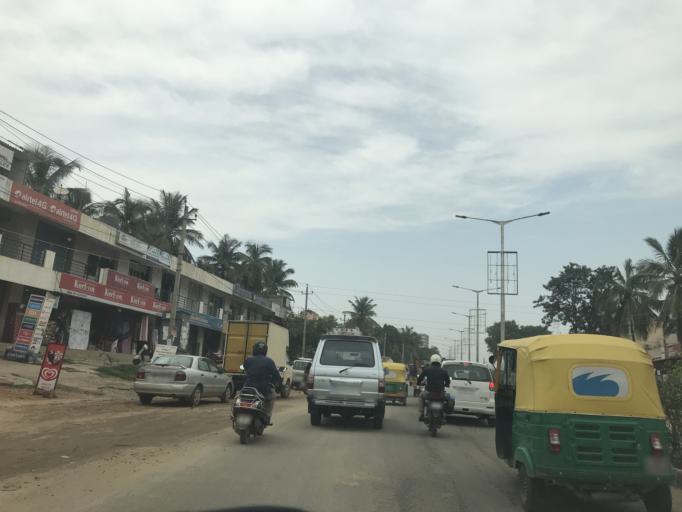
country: IN
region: Karnataka
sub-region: Bangalore Urban
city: Yelahanka
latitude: 13.0493
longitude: 77.6455
